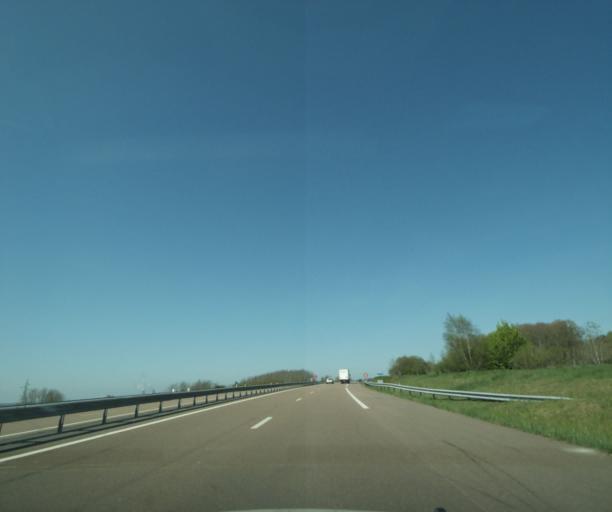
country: FR
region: Bourgogne
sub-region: Departement de la Nievre
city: Cosne-Cours-sur-Loire
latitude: 47.4315
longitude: 2.9390
